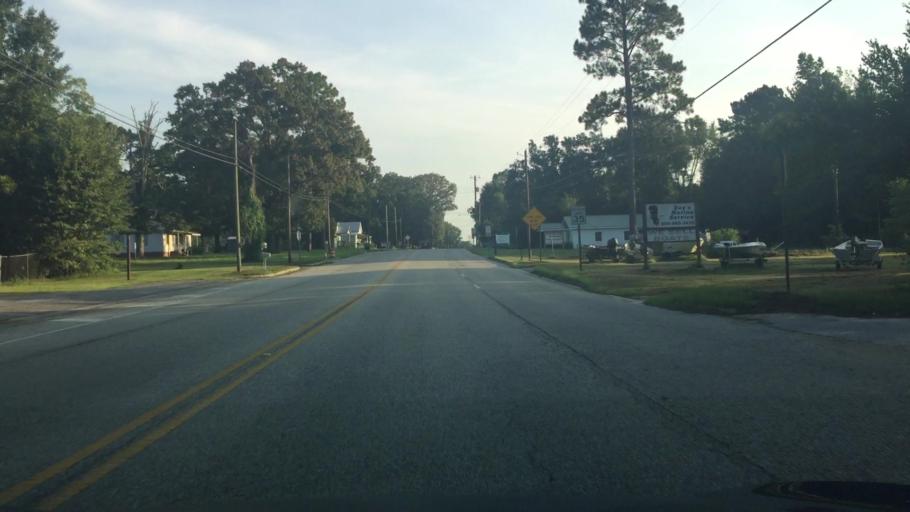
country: US
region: Alabama
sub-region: Covington County
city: Florala
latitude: 30.9944
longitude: -86.3091
